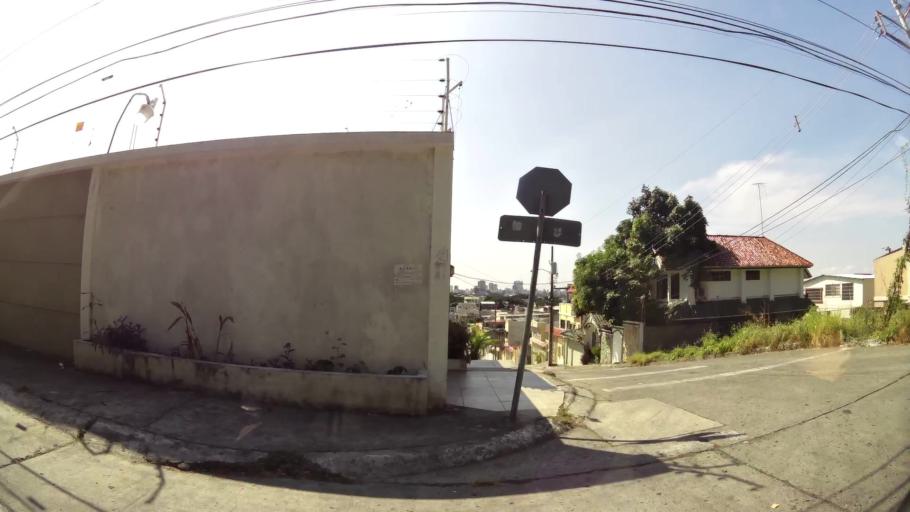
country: EC
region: Guayas
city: Guayaquil
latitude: -2.1867
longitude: -79.9167
